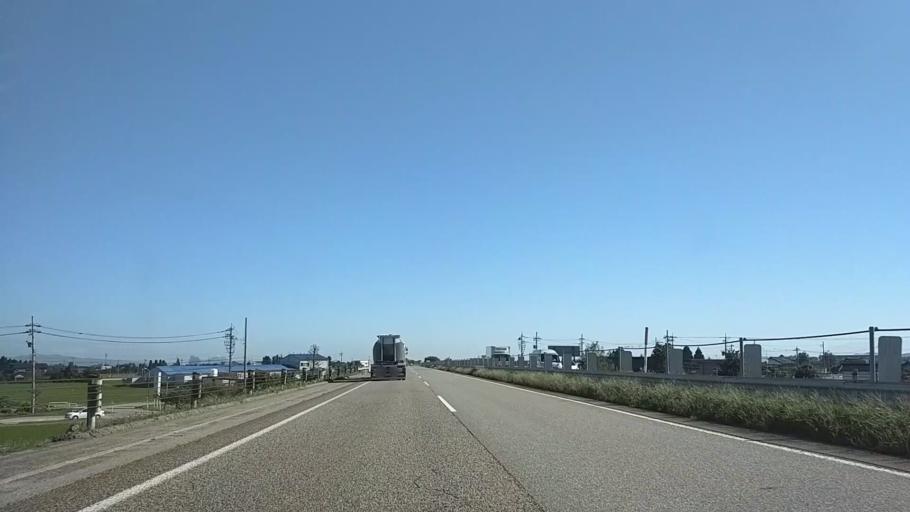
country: JP
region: Toyama
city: Nanto-shi
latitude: 36.6359
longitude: 136.9697
